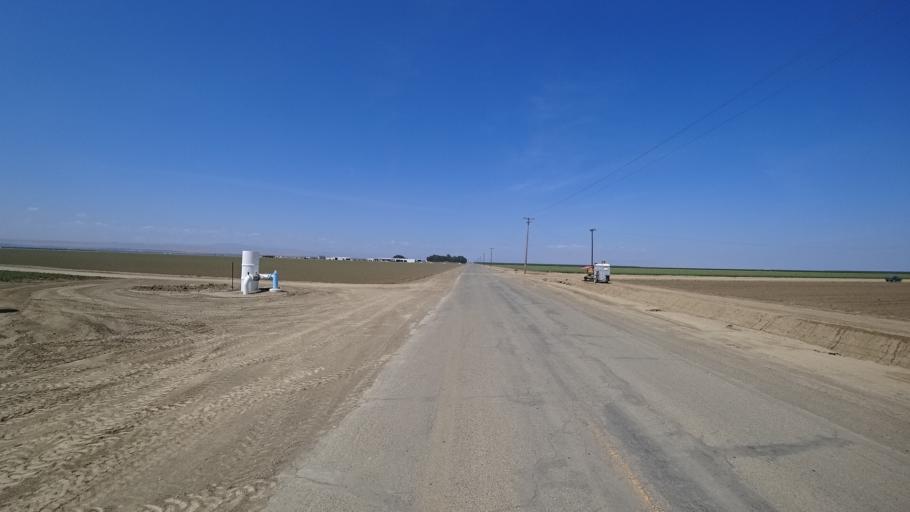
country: US
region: California
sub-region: Kings County
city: Kettleman City
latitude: 36.1377
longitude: -119.9766
